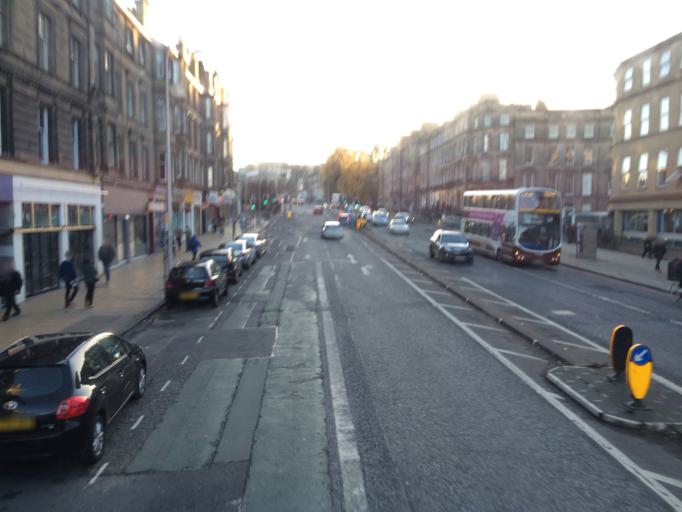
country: GB
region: Scotland
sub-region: Edinburgh
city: Edinburgh
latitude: 55.9601
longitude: -3.1822
